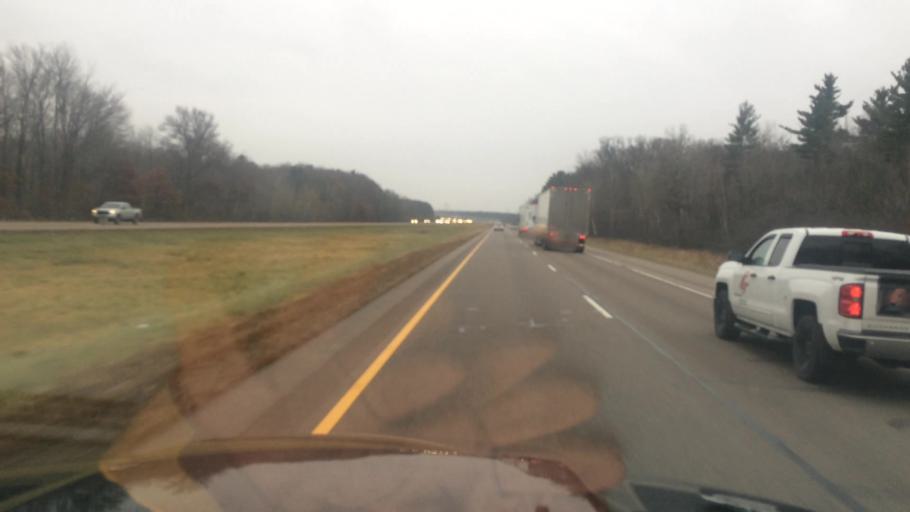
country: US
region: Wisconsin
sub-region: Portage County
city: Stevens Point
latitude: 44.5836
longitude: -89.6073
